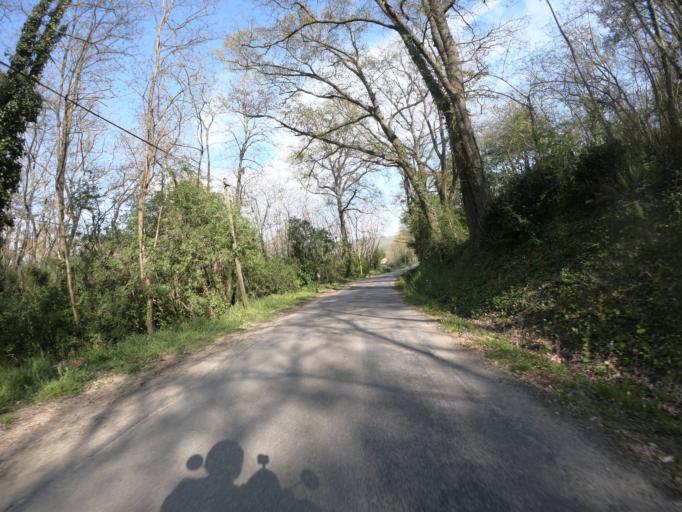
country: FR
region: Midi-Pyrenees
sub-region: Departement de l'Ariege
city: La Tour-du-Crieu
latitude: 43.1108
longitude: 1.7173
